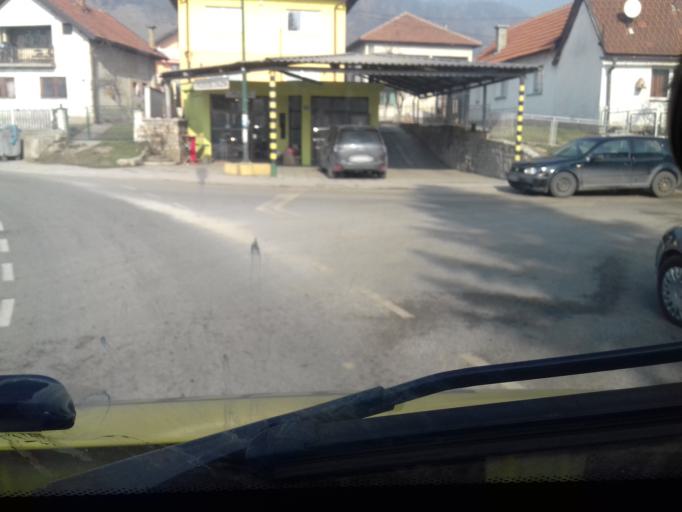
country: BA
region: Federation of Bosnia and Herzegovina
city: Ilijas
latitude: 43.9508
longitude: 18.2704
